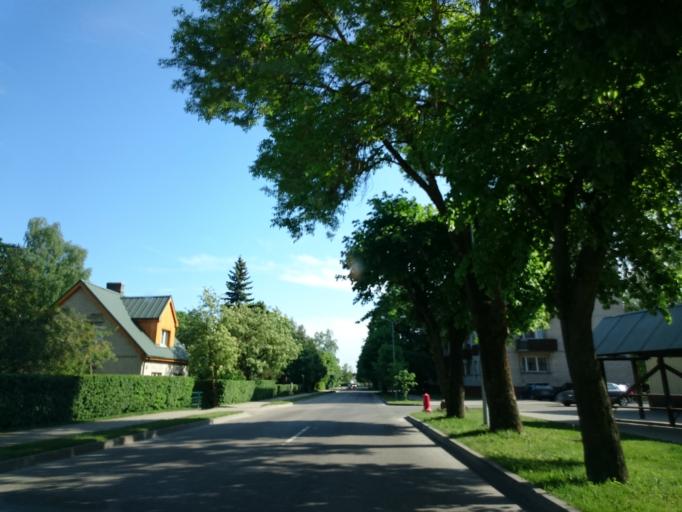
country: LV
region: Dobeles Rajons
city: Dobele
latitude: 56.6165
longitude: 23.2836
